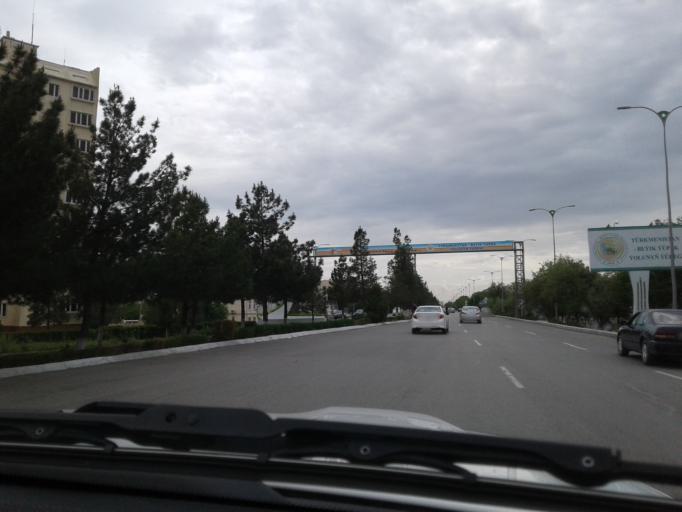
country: TM
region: Mary
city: Mary
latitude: 37.5946
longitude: 61.8764
